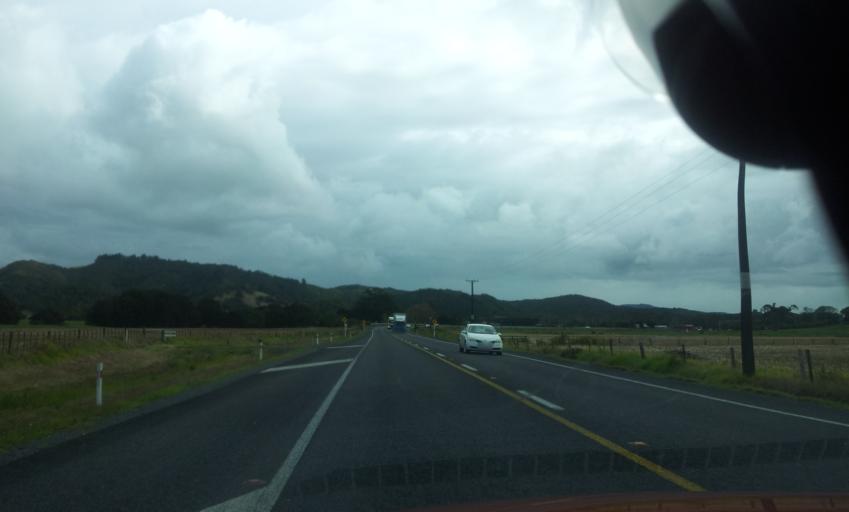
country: NZ
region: Northland
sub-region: Whangarei
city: Ruakaka
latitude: -36.0066
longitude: 174.4160
